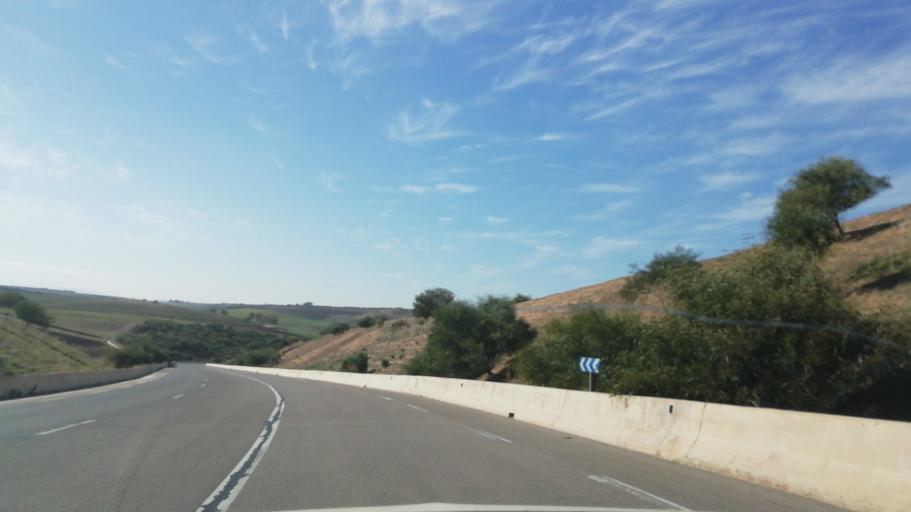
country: DZ
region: Tlemcen
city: Chetouane
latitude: 34.9819
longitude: -1.2299
